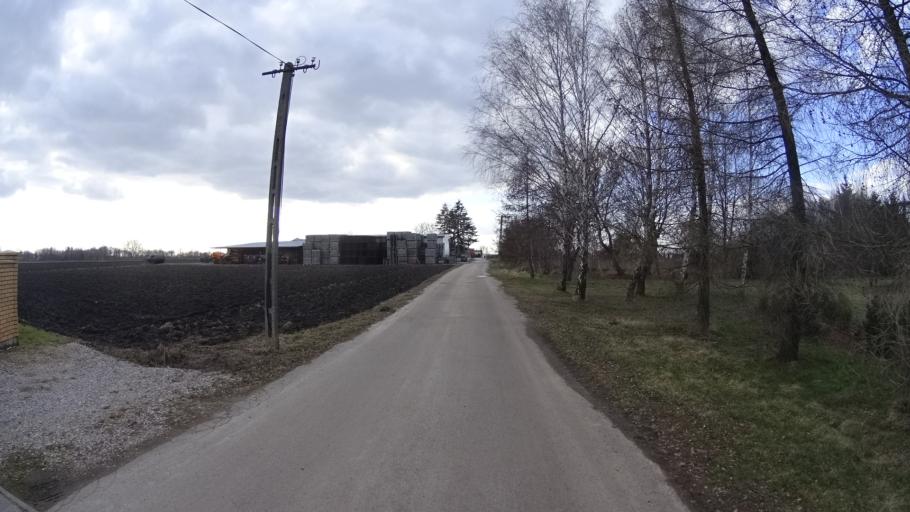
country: PL
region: Masovian Voivodeship
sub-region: Powiat warszawski zachodni
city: Ozarow Mazowiecki
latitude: 52.2455
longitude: 20.7905
